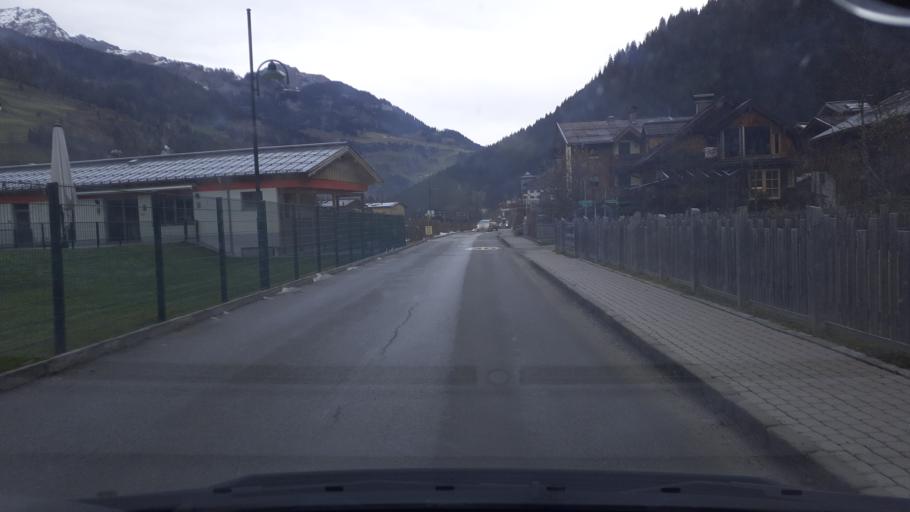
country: AT
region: Salzburg
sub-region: Politischer Bezirk Sankt Johann im Pongau
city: Huttschlag
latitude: 47.2428
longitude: 13.1999
